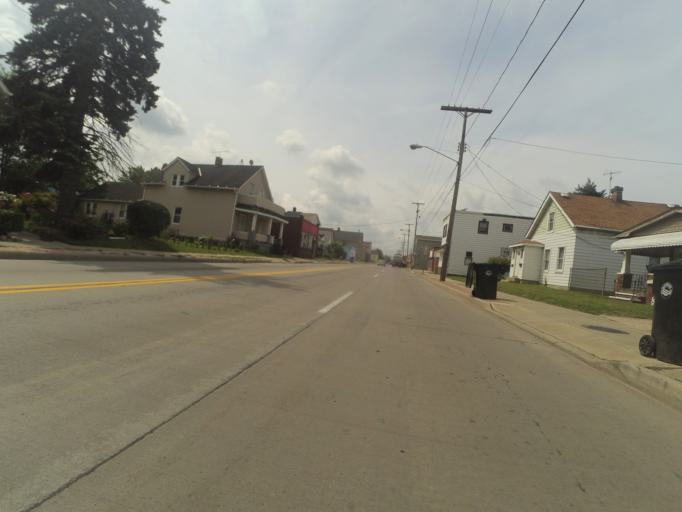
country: US
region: Ohio
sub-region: Cuyahoga County
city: Cleveland
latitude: 41.4657
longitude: -81.7083
